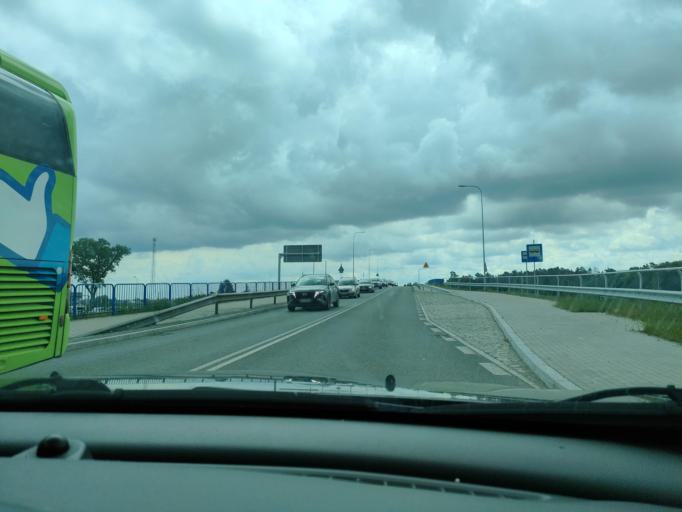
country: PL
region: Kujawsko-Pomorskie
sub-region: Powiat bydgoski
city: Osielsko
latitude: 53.2241
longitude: 18.1261
